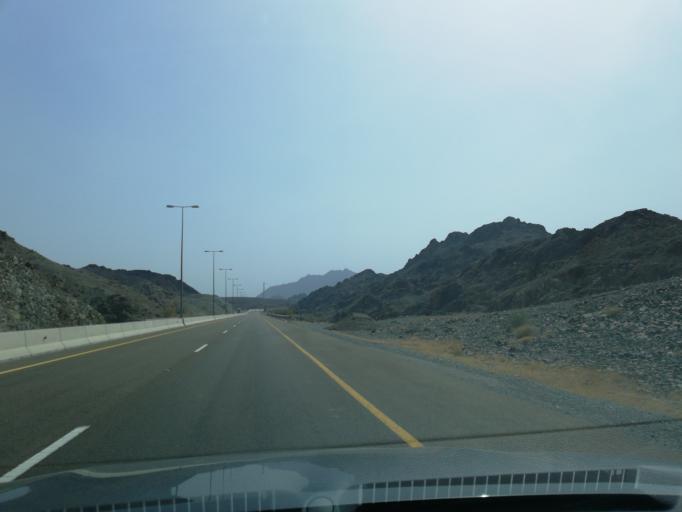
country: OM
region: Al Batinah
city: Al Liwa'
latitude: 24.2658
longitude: 56.3847
